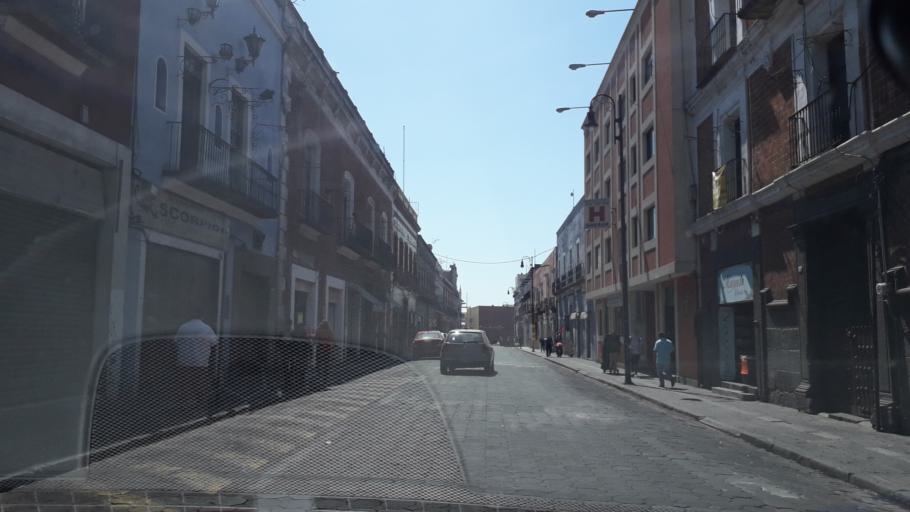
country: MX
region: Puebla
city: Puebla
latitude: 19.0458
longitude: -98.1937
